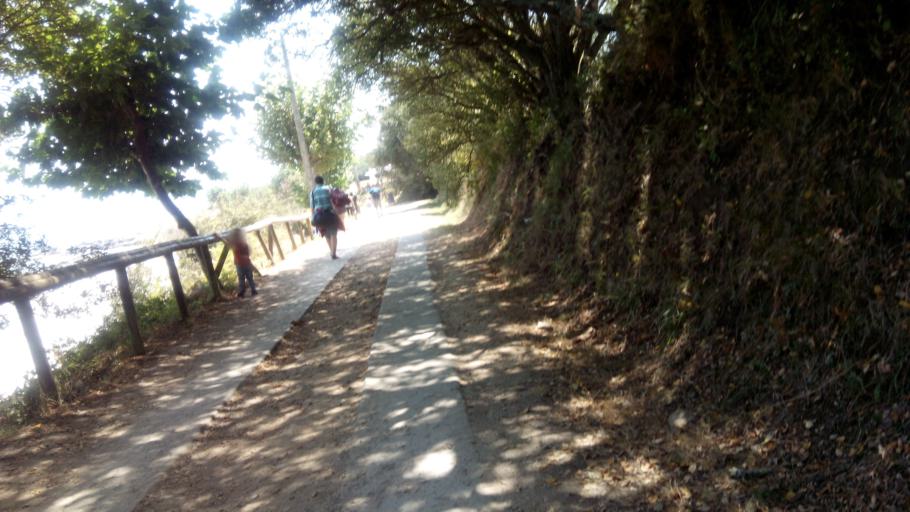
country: ES
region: Galicia
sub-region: Provincia de Pontevedra
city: Sanxenxo
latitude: 42.3745
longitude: -8.9334
